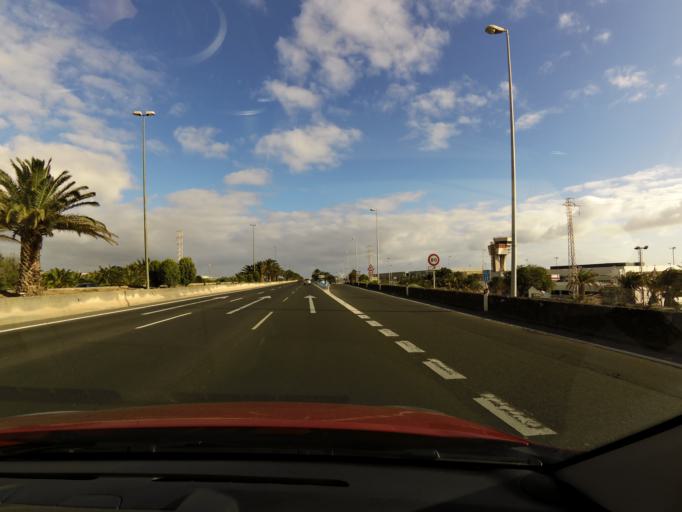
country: ES
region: Canary Islands
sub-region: Provincia de Las Palmas
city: Ingenio
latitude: 27.9342
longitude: -15.3933
